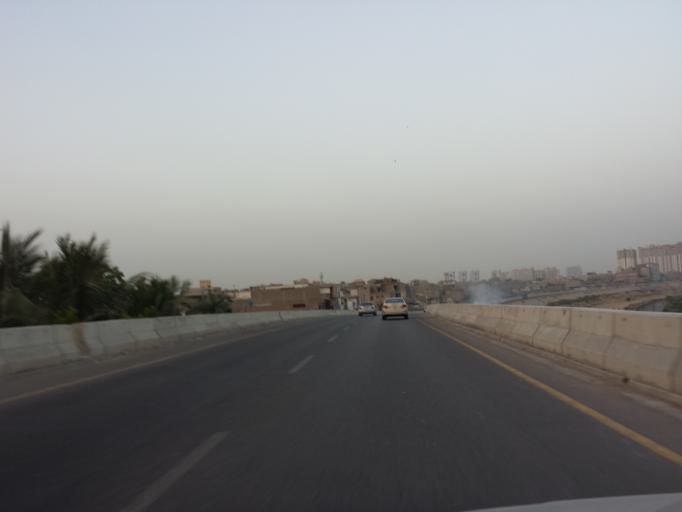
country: PK
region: Sindh
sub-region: Karachi District
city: Karachi
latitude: 24.9080
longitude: 67.0641
